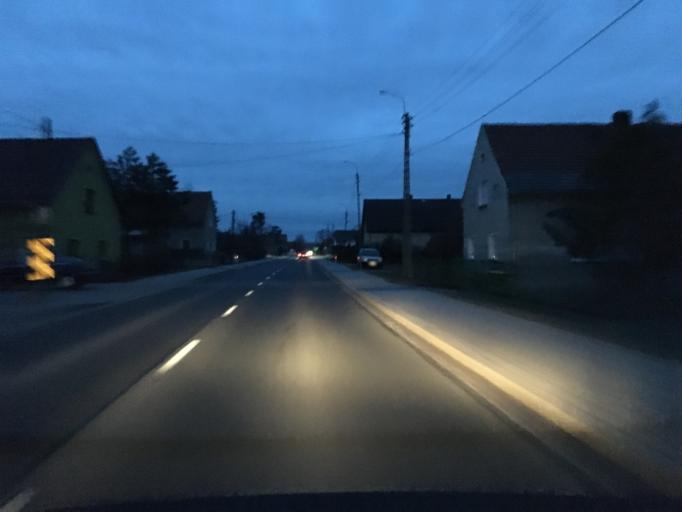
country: PL
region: Opole Voivodeship
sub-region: Powiat brzeski
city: Losiow
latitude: 50.7889
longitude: 17.5744
